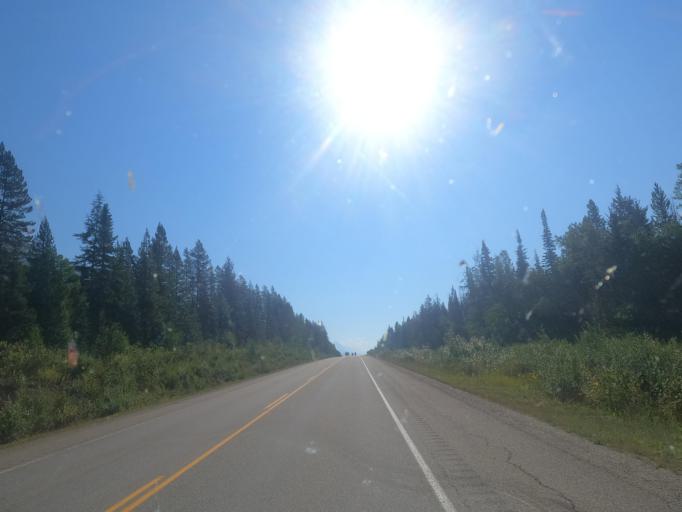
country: CA
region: Alberta
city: Jasper Park Lodge
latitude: 52.9776
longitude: -118.9681
